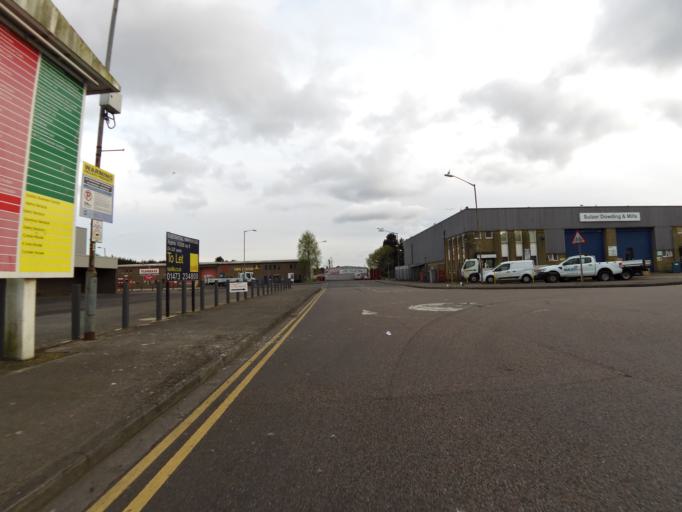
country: GB
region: England
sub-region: Suffolk
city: Kesgrave
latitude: 52.0300
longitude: 1.2043
